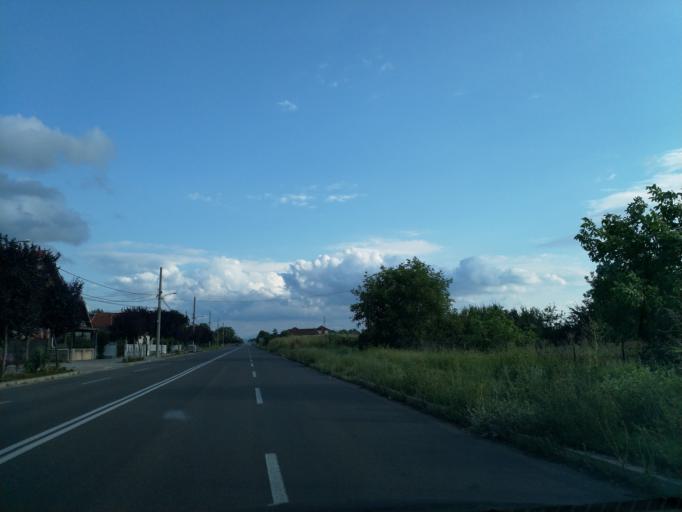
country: RS
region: Central Serbia
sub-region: Pomoravski Okrug
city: Paracin
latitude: 43.8403
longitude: 21.4152
